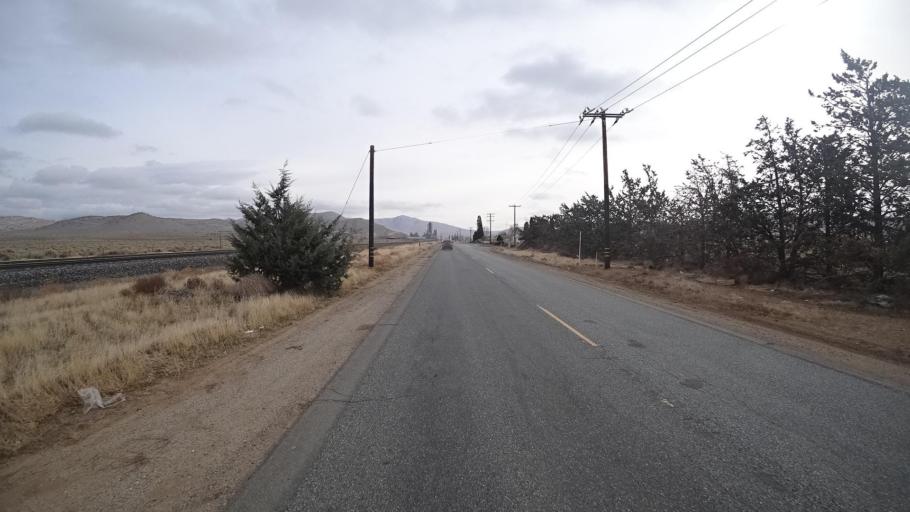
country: US
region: California
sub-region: Kern County
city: Tehachapi
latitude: 35.1245
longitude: -118.3909
